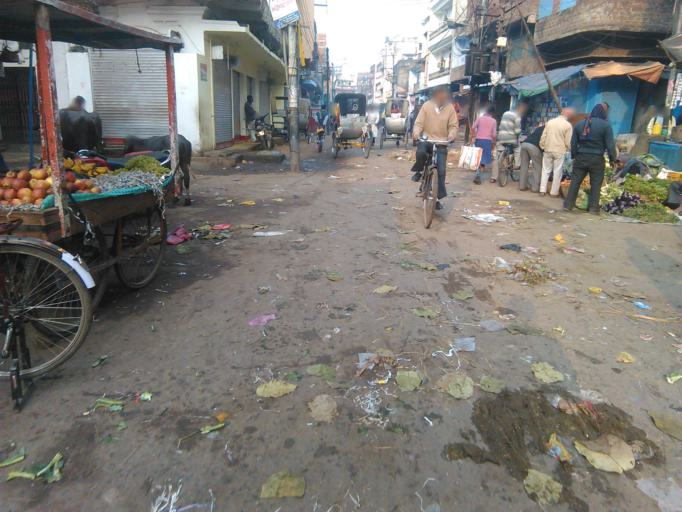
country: IN
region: Bihar
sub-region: Gaya
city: Gaya
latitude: 24.7978
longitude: 85.0050
